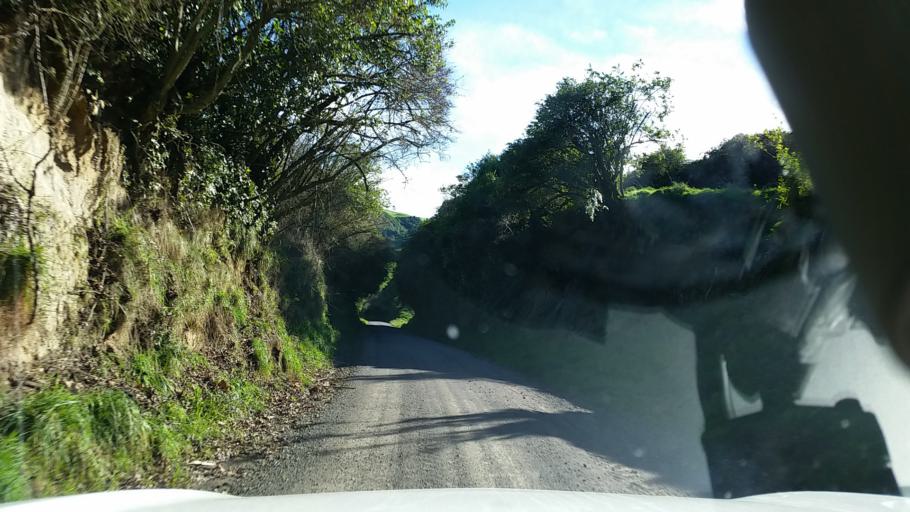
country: NZ
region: Waikato
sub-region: Taupo District
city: Taupo
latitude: -38.4324
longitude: 176.1585
